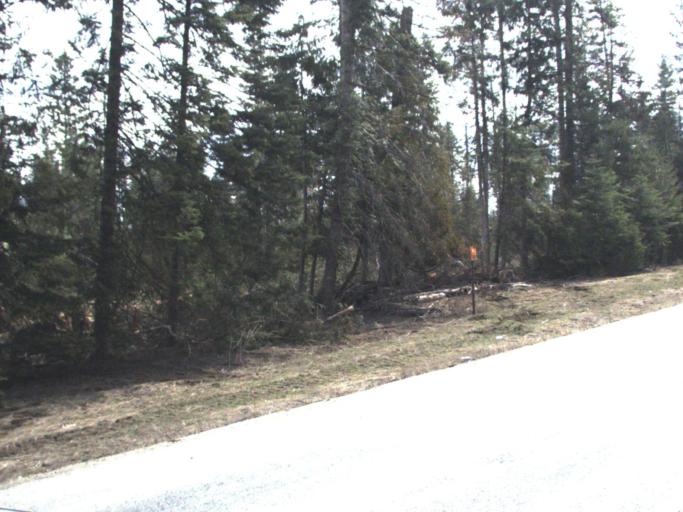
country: US
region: Washington
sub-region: Pend Oreille County
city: Newport
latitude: 48.2845
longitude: -117.2701
